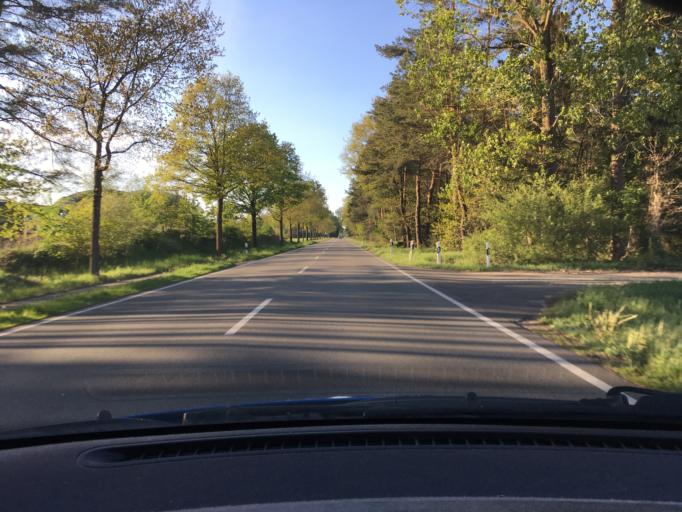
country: DE
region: Lower Saxony
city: Oldendorf
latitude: 53.1648
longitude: 10.2122
